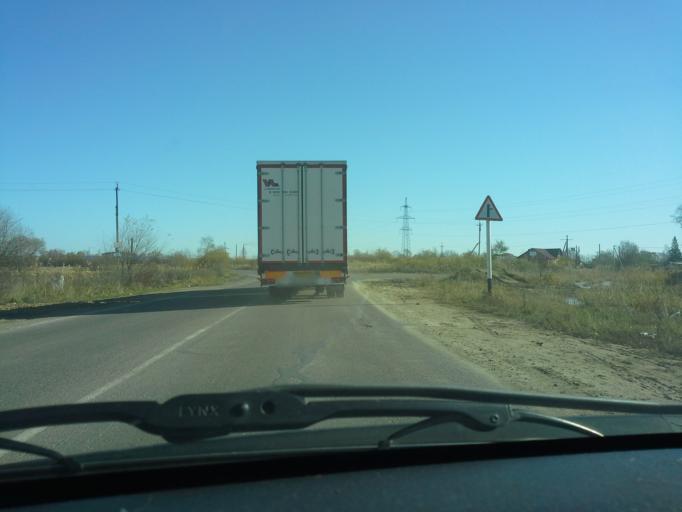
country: RU
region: Jewish Autonomous Oblast
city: Priamurskiy
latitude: 48.5285
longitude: 134.8887
